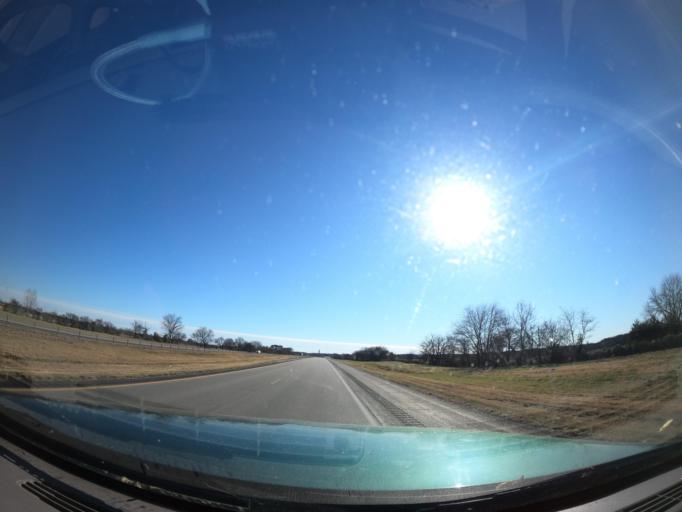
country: US
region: Oklahoma
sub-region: McIntosh County
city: Checotah
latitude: 35.4267
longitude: -95.5567
